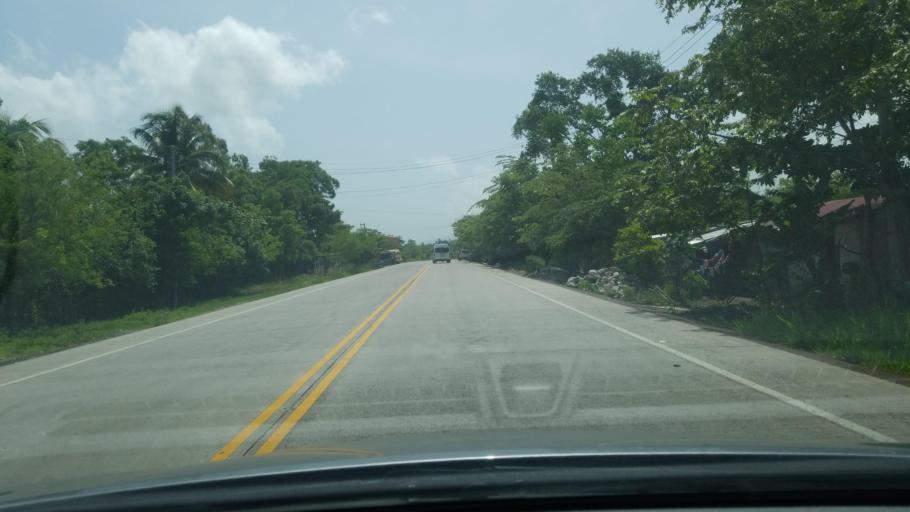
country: HN
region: Copan
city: Florida
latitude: 15.0457
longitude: -88.8088
